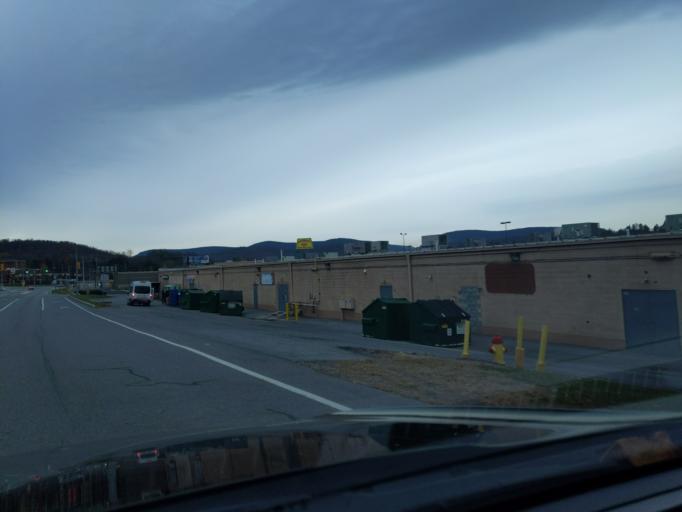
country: US
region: Pennsylvania
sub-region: Blair County
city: Lakemont
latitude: 40.4695
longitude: -78.4040
